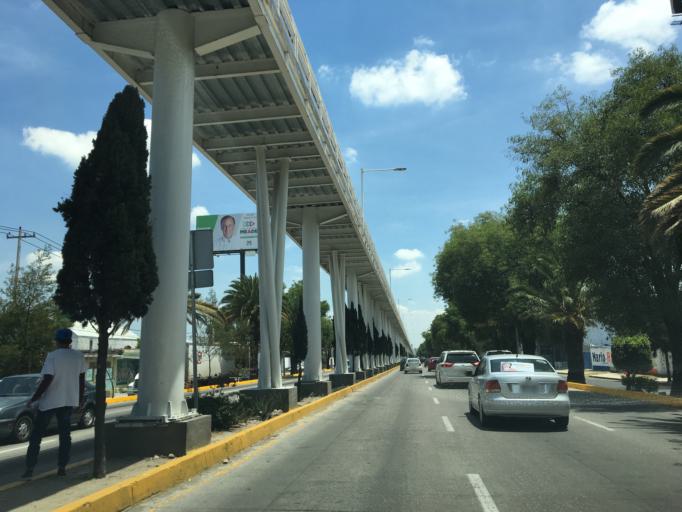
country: MX
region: Puebla
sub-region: Cuautlancingo
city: Sanctorum
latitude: 19.0800
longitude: -98.2282
